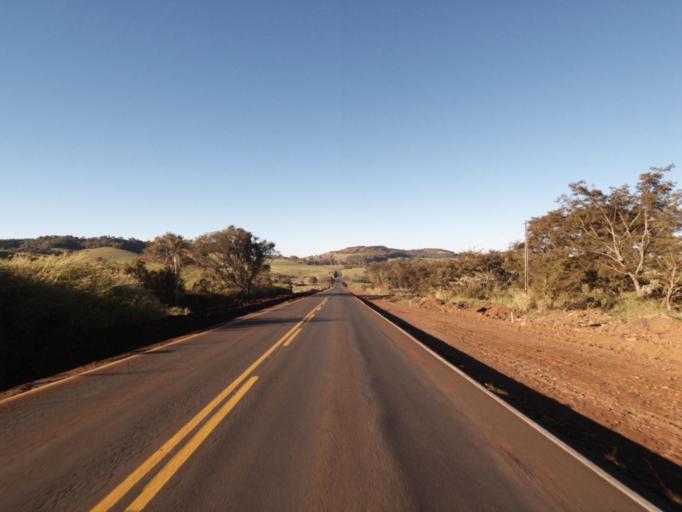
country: AR
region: Misiones
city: Bernardo de Irigoyen
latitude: -26.3609
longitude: -53.5353
